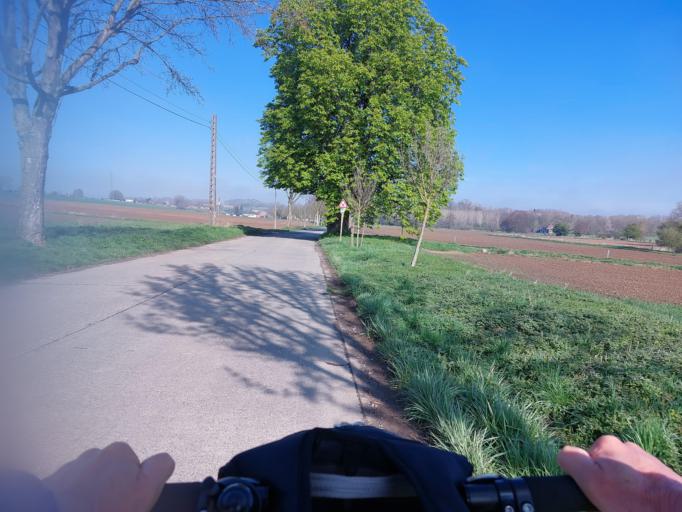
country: BE
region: Wallonia
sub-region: Province du Hainaut
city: Chasse Royale
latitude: 50.4041
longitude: 3.9774
